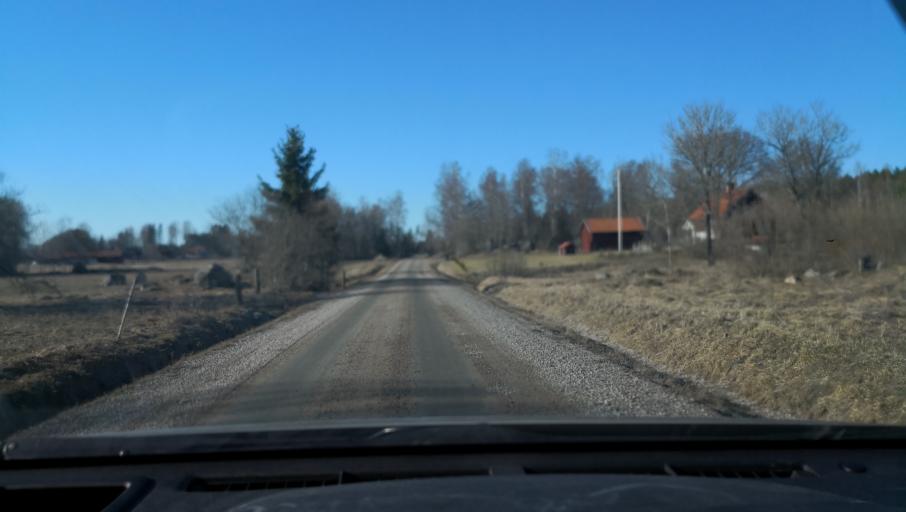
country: SE
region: Vaestmanland
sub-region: Sala Kommun
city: Sala
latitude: 60.1701
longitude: 16.6341
